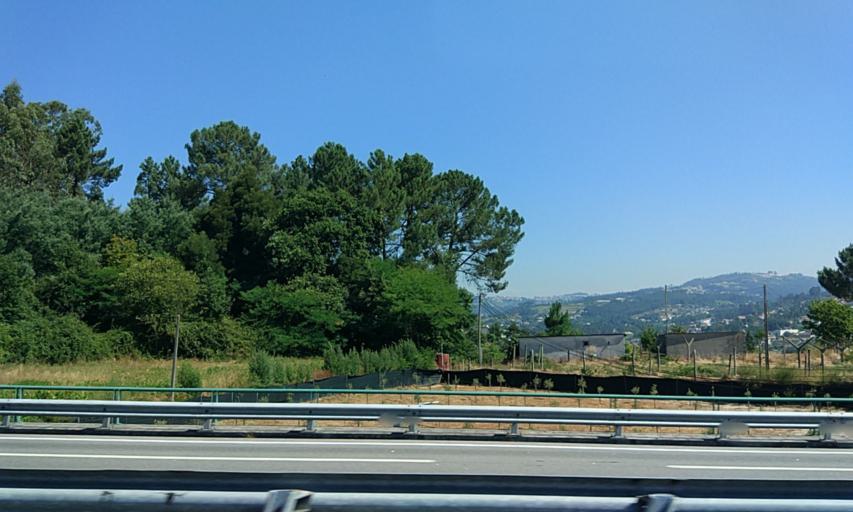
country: PT
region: Porto
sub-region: Marco de Canaveses
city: Marco de Canavezes
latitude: 41.2301
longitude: -8.1895
